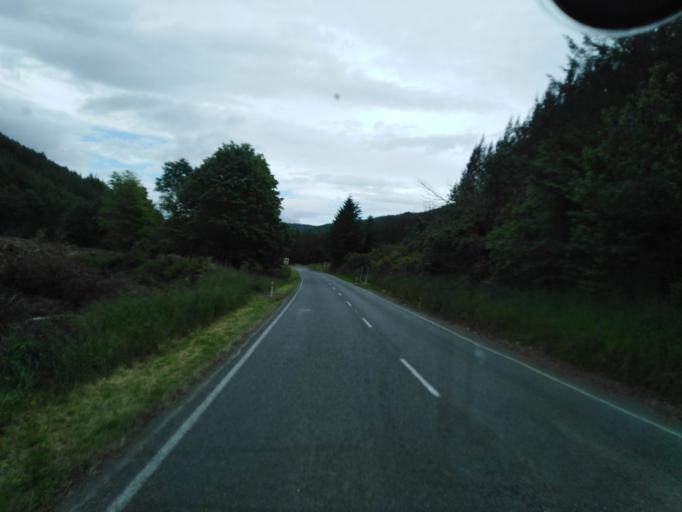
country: NZ
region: Tasman
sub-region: Tasman District
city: Wakefield
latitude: -41.4856
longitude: 172.8883
